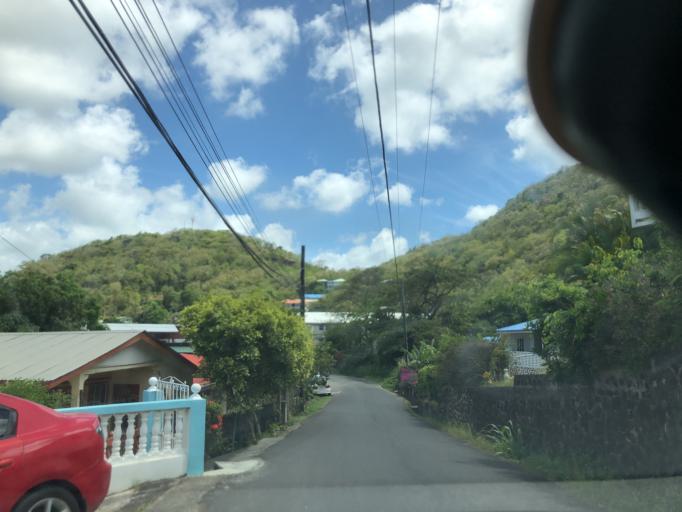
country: LC
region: Gros-Islet
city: Gros Islet
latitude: 14.0601
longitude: -60.9671
